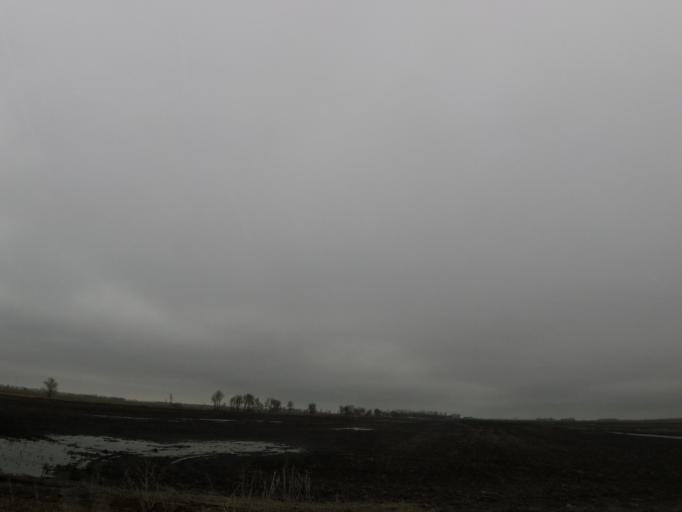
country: US
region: North Dakota
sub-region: Walsh County
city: Grafton
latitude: 48.3830
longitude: -97.2244
